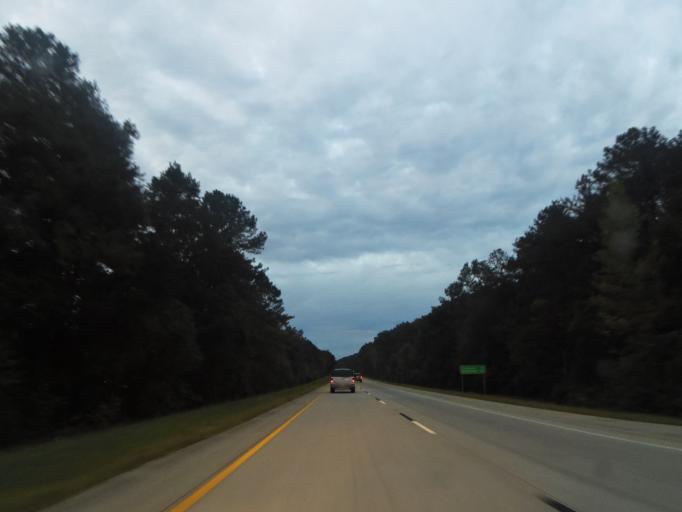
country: US
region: Alabama
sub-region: Etowah County
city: Gadsden
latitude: 34.0810
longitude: -86.0194
